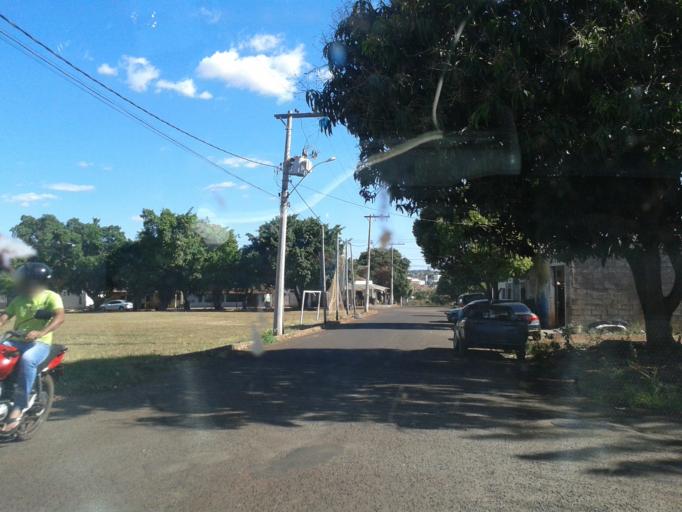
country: BR
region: Minas Gerais
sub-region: Ituiutaba
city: Ituiutaba
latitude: -18.9583
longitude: -49.4599
